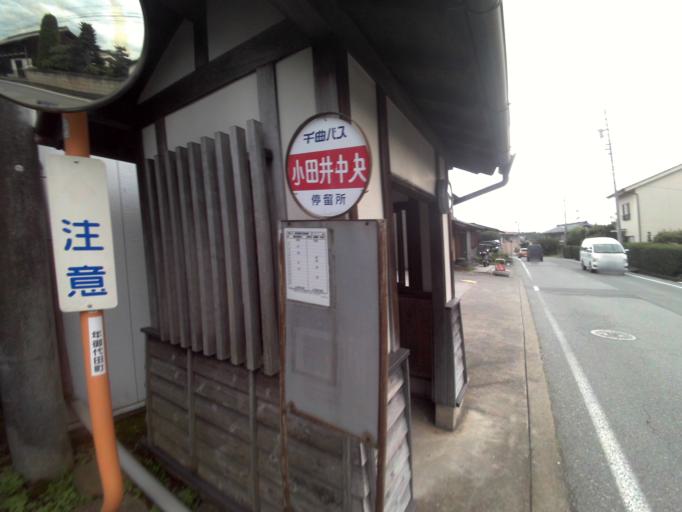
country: JP
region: Nagano
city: Komoro
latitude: 36.3052
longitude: 138.4958
